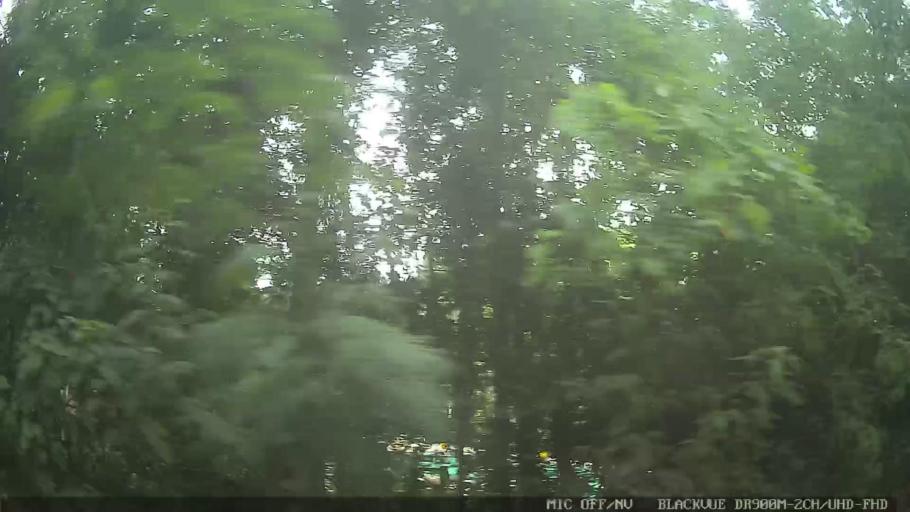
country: BR
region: Sao Paulo
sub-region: Atibaia
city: Atibaia
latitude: -23.1540
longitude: -46.5161
